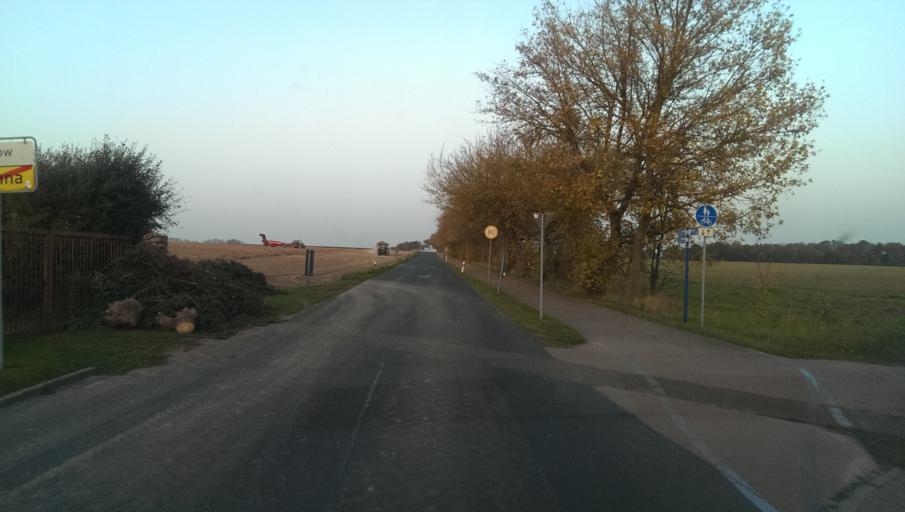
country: DE
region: Brandenburg
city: Juterbog
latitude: 51.9330
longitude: 13.0503
